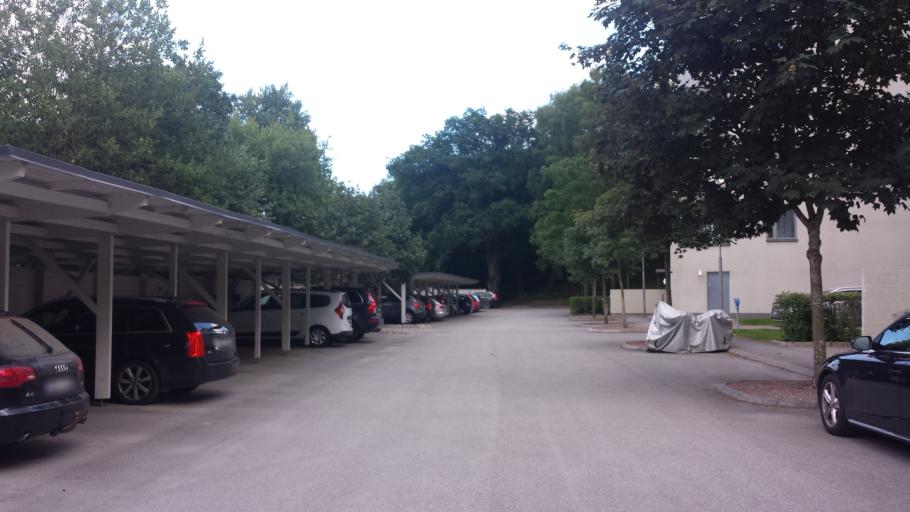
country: SE
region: Stockholm
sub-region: Solna Kommun
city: Solna
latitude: 59.3542
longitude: 18.0072
